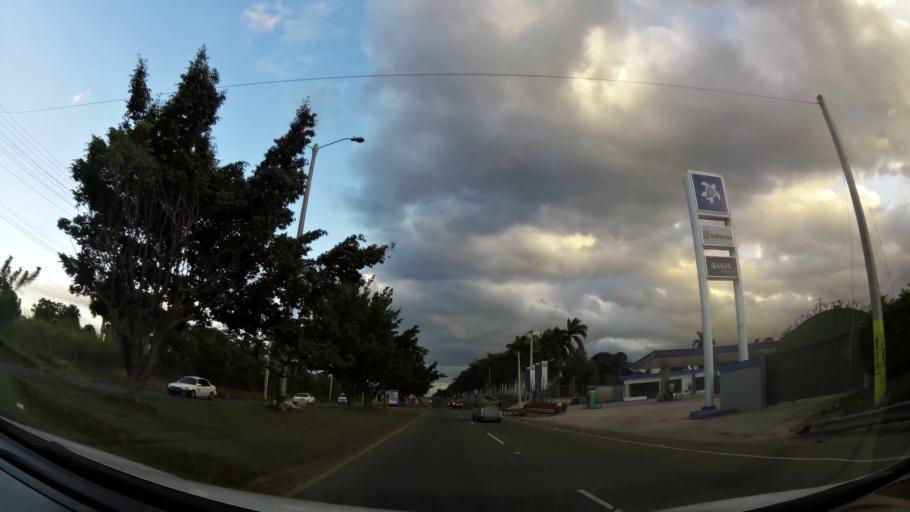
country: DO
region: Santiago
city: Licey al Medio
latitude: 19.4032
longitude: -70.6345
